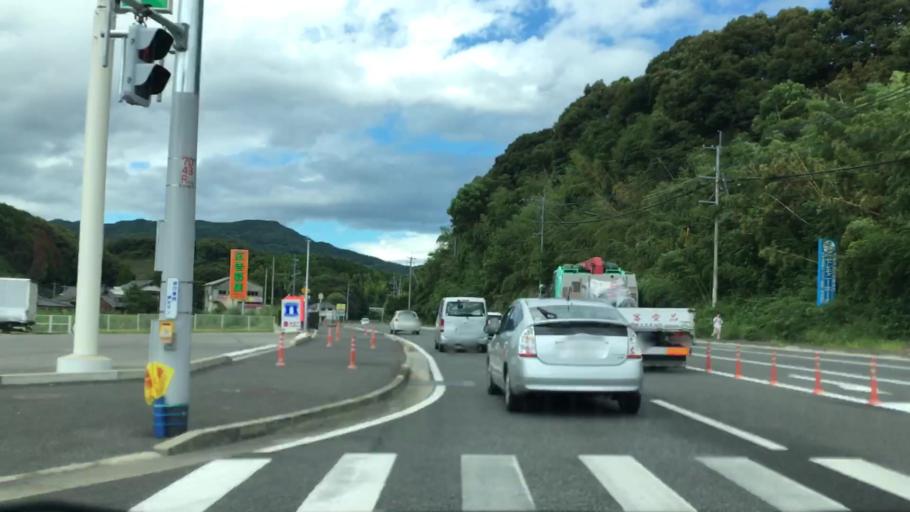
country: JP
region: Saga Prefecture
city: Imaricho-ko
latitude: 33.2775
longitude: 129.8949
